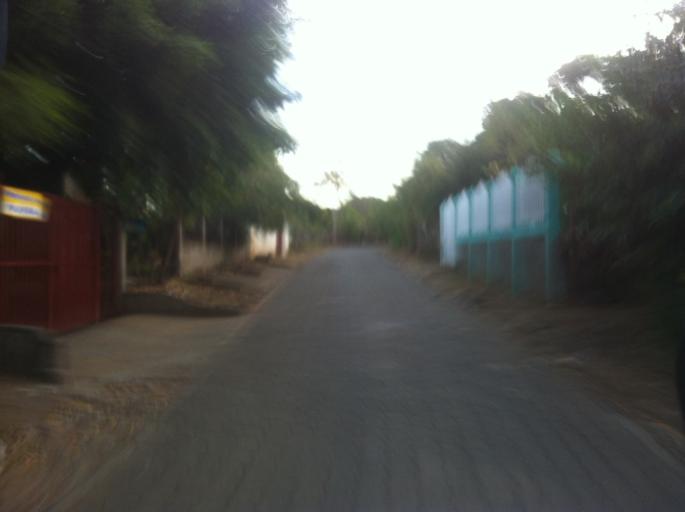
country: NI
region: Managua
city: Ciudad Sandino
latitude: 12.0886
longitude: -86.3341
